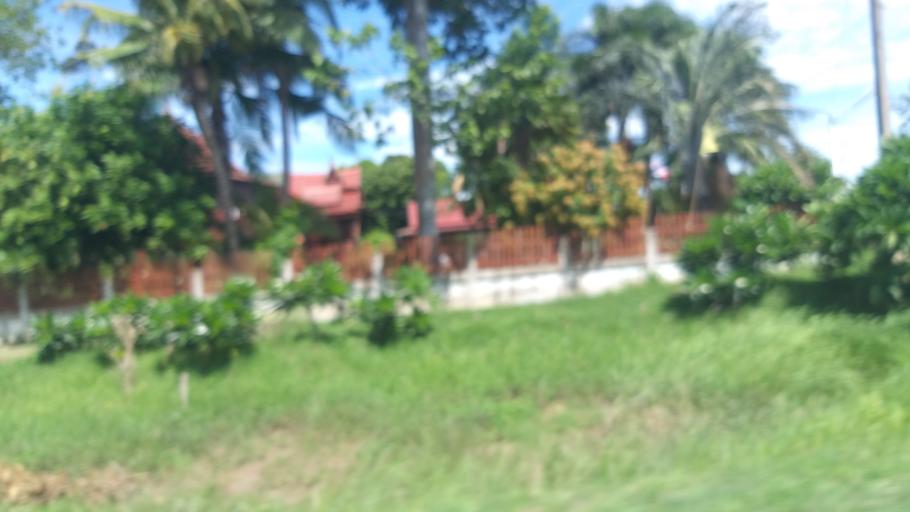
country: TH
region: Khon Kaen
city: Nong Ruea
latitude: 16.4614
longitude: 102.4414
